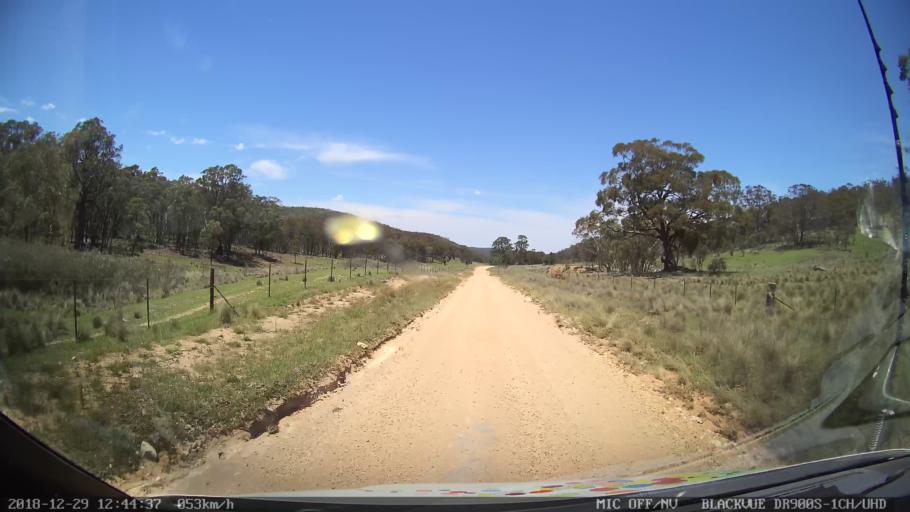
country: AU
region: Australian Capital Territory
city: Macarthur
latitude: -35.6287
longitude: 149.2159
